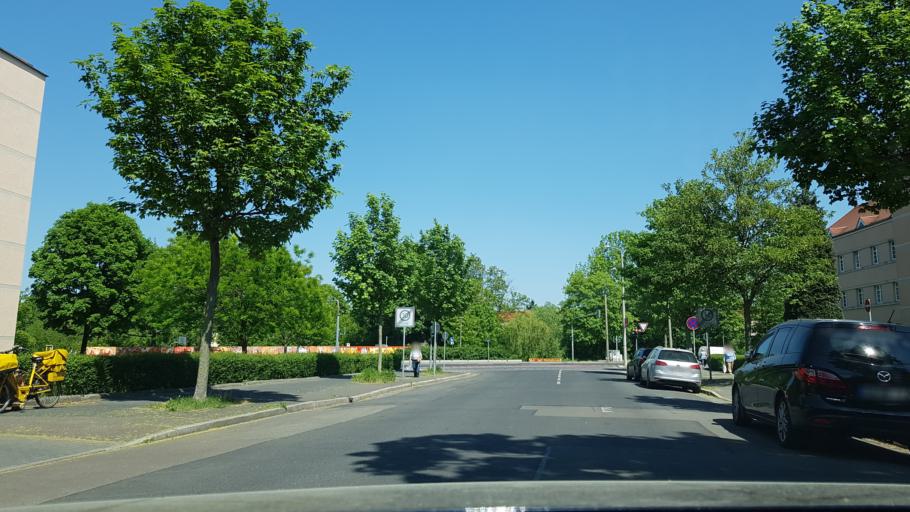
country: DE
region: Saxony
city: Dresden
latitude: 51.0209
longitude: 13.7635
